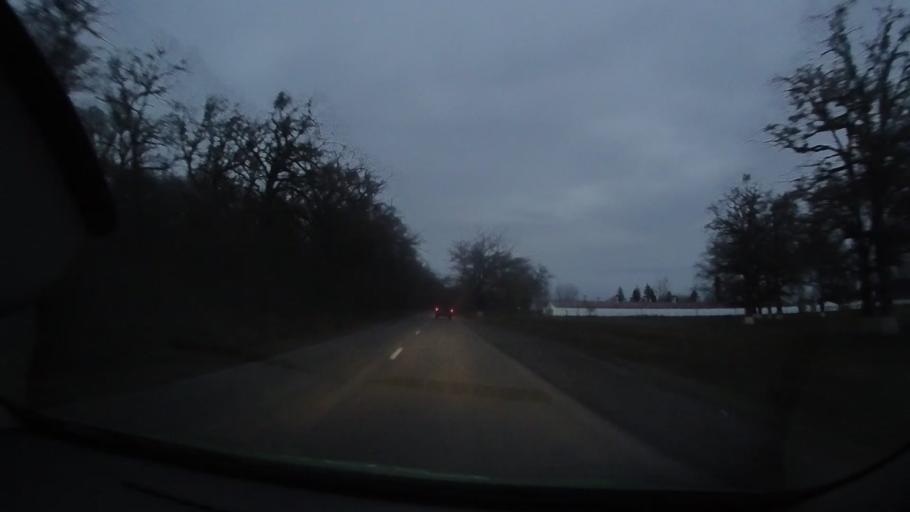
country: RO
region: Mures
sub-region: Comuna Solovastru
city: Jabenita
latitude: 46.7710
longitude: 24.8208
